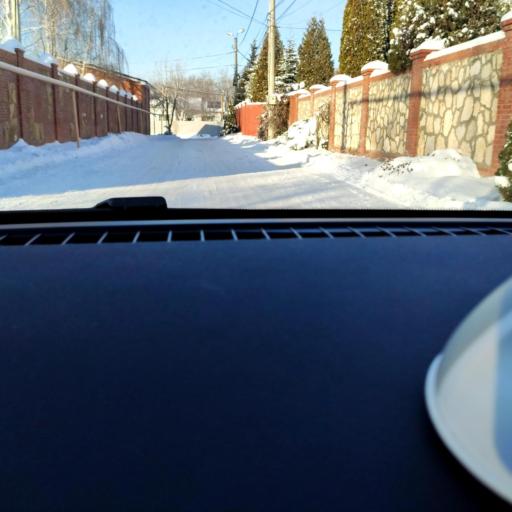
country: RU
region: Samara
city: Samara
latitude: 53.2774
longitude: 50.2044
